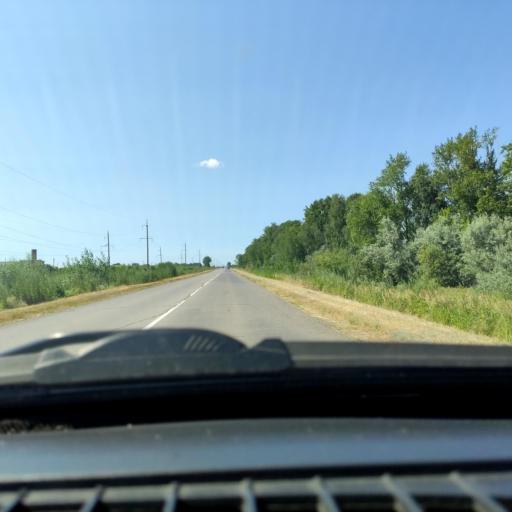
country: RU
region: Samara
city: Tol'yatti
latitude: 53.7289
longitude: 49.4149
